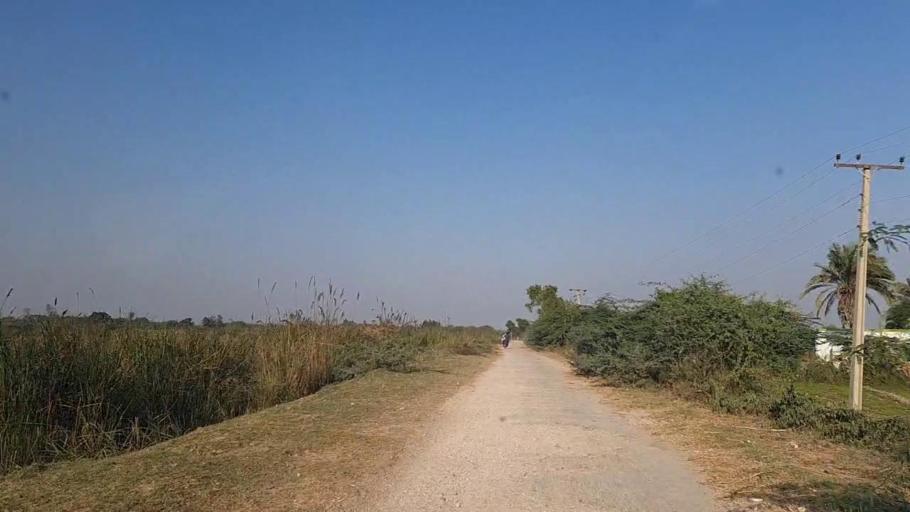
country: PK
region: Sindh
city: Thatta
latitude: 24.7172
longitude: 67.9415
